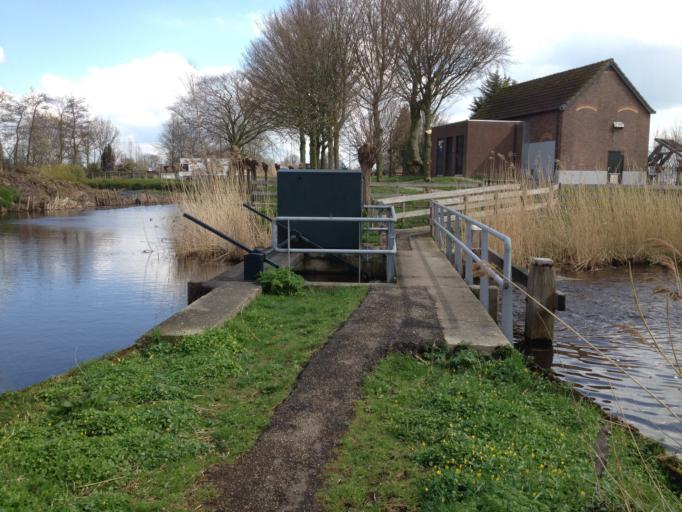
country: NL
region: South Holland
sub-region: Gemeente Boskoop
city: Boskoop
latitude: 52.0864
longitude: 4.6459
